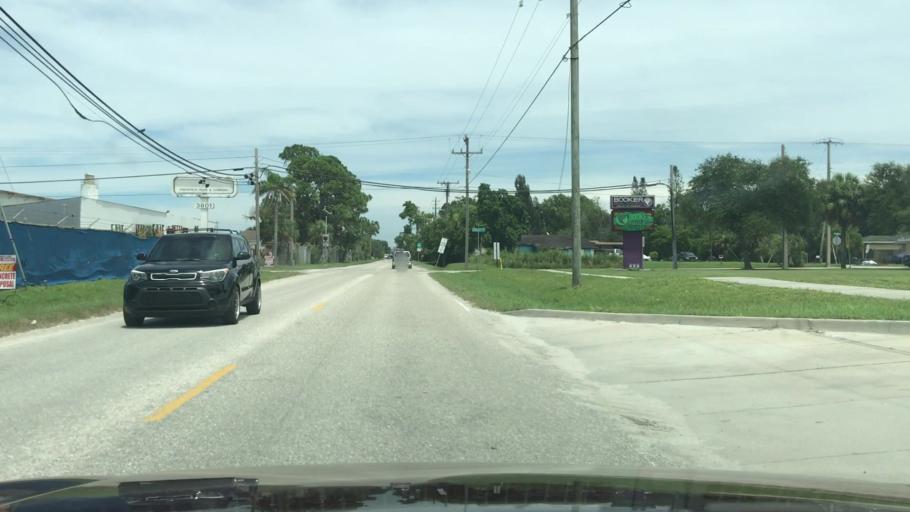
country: US
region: Florida
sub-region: Sarasota County
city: North Sarasota
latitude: 27.3671
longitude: -82.5396
